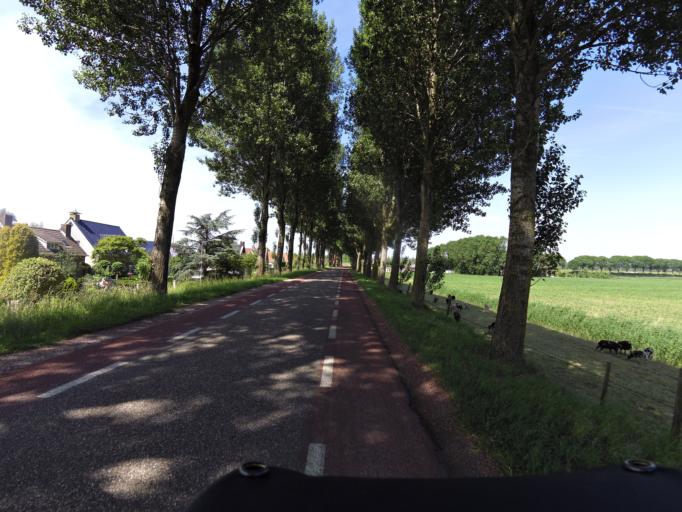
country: NL
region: North Brabant
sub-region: Gemeente Moerdijk
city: Klundert
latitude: 51.6765
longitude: 4.4946
